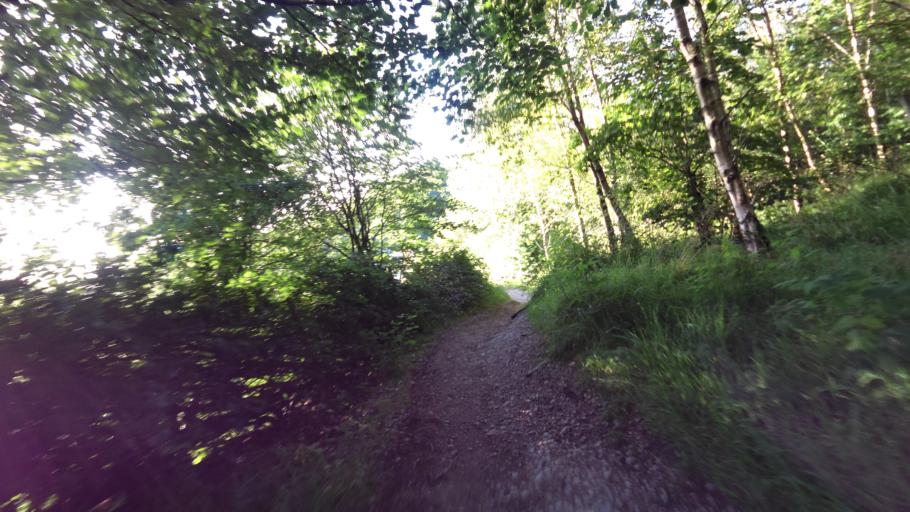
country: GB
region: England
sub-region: Lancashire
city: Clitheroe
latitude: 53.9995
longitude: -2.4018
